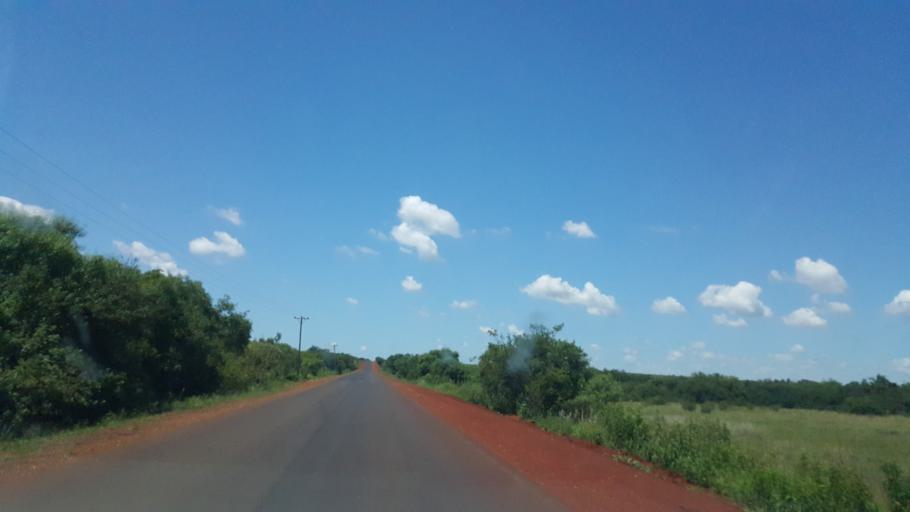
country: AR
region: Corrientes
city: Santo Tome
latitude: -28.4683
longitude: -56.0262
